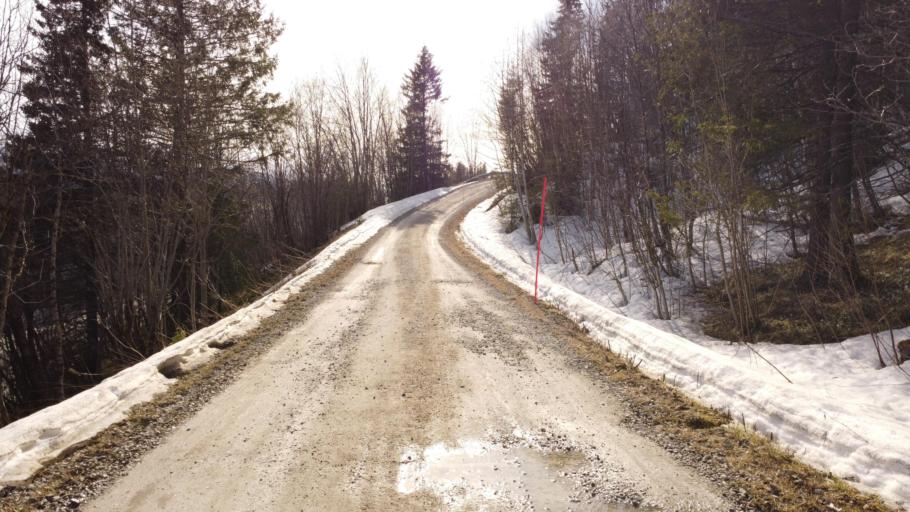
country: NO
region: Nordland
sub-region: Rana
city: Mo i Rana
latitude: 66.3307
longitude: 14.1643
